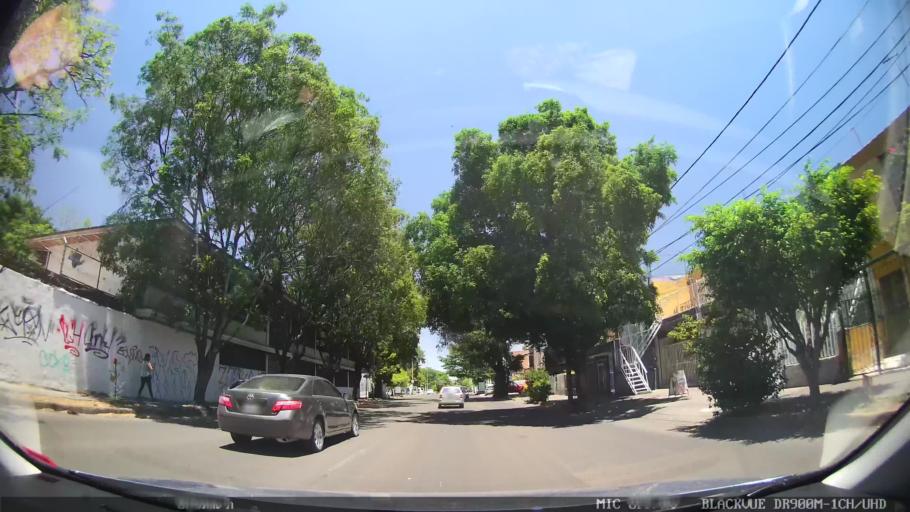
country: MX
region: Jalisco
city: Tlaquepaque
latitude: 20.6621
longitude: -103.2832
